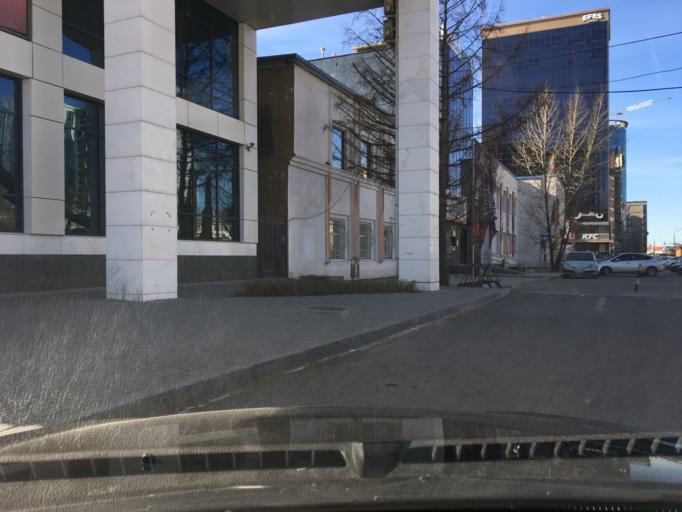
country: MN
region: Ulaanbaatar
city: Ulaanbaatar
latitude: 47.8988
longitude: 106.8997
